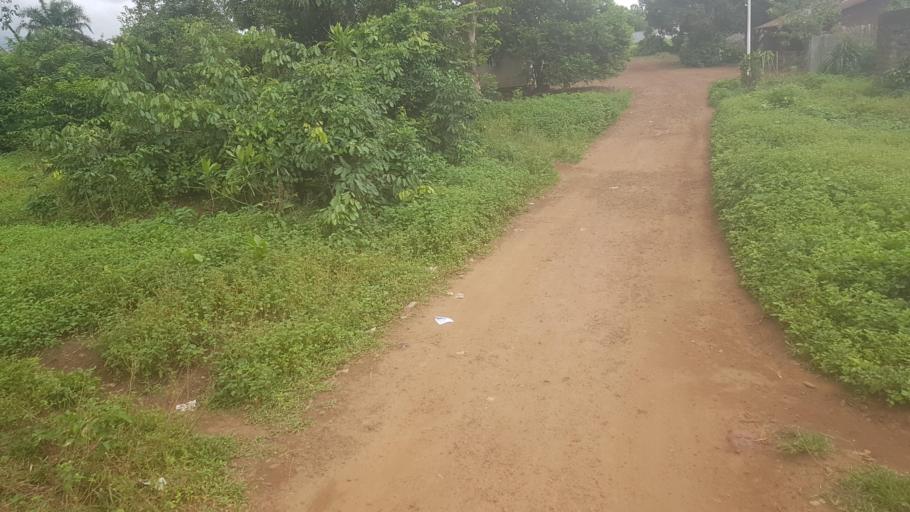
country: SL
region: Southern Province
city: Mogbwemo
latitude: 7.6130
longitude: -12.1771
